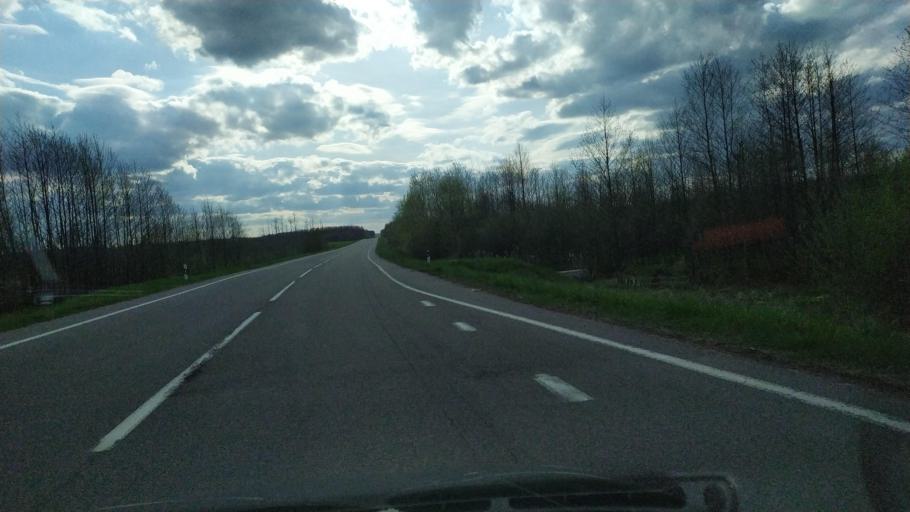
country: BY
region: Brest
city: Pruzhany
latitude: 52.6973
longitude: 24.2680
